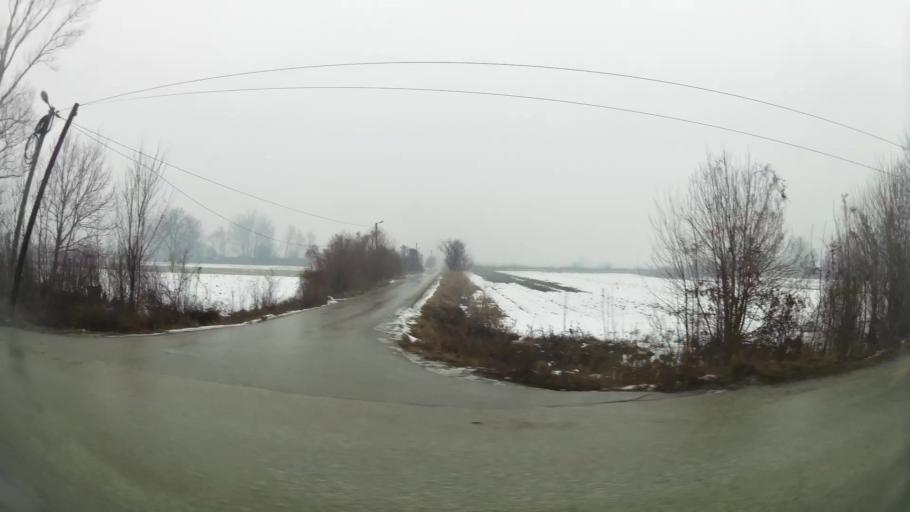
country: MK
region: Petrovec
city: Petrovec
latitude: 41.9464
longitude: 21.5959
